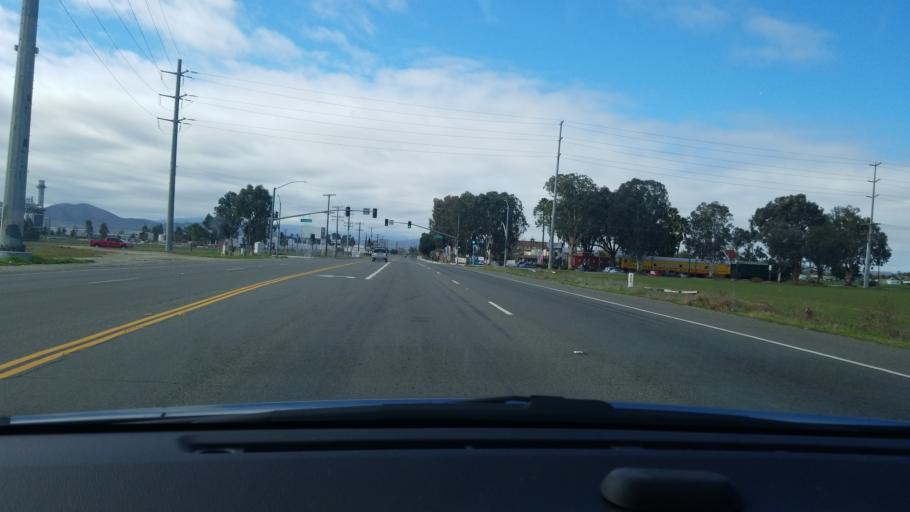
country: US
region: California
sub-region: Riverside County
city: Romoland
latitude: 33.7430
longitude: -117.1618
